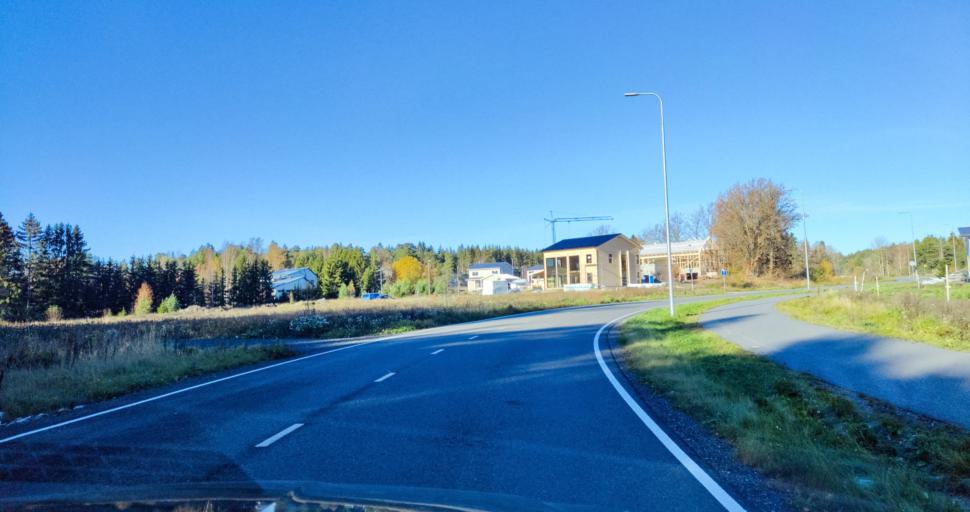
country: FI
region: Varsinais-Suomi
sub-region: Turku
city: Turku
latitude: 60.4052
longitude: 22.2088
